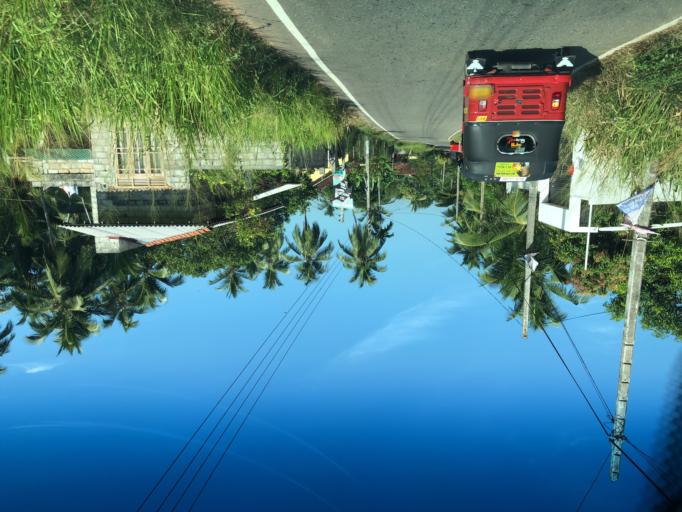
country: LK
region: Western
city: Homagama
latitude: 6.8024
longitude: 79.9804
